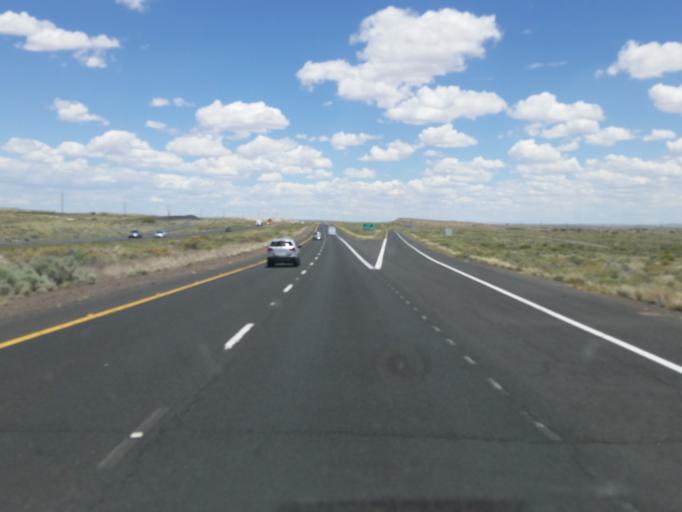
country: US
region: Arizona
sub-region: Navajo County
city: Holbrook
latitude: 34.9908
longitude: -109.9663
